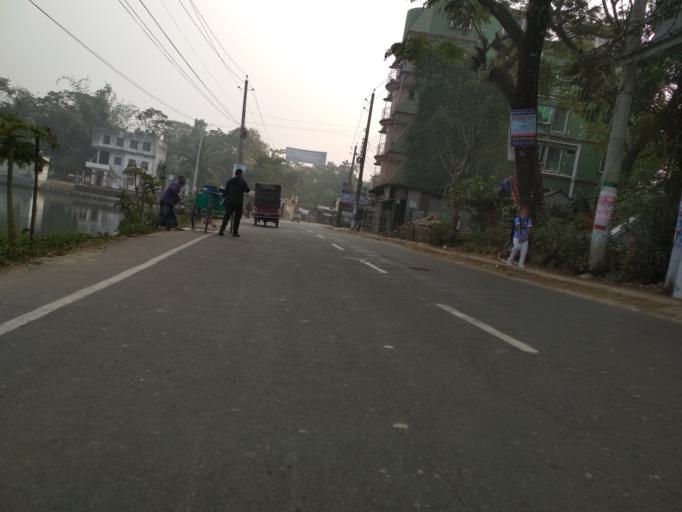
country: BD
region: Chittagong
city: Lakshmipur
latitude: 22.9382
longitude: 90.8414
